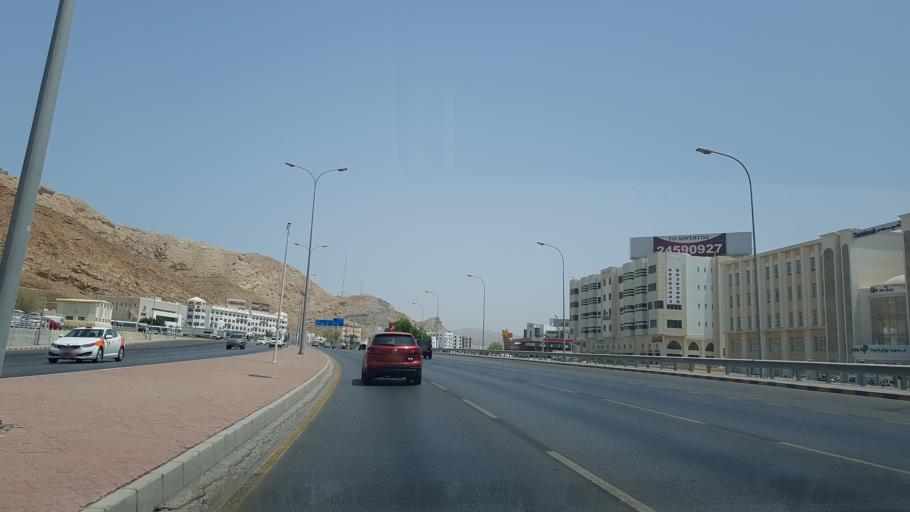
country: OM
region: Muhafazat Masqat
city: Muscat
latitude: 23.6013
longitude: 58.5154
